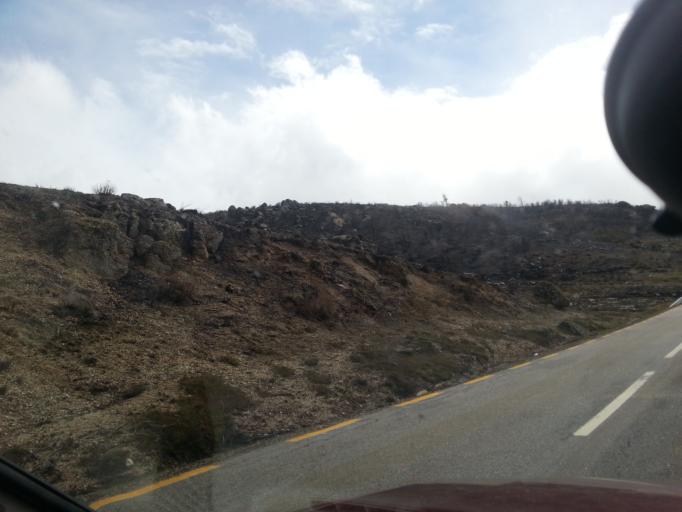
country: PT
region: Guarda
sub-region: Manteigas
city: Manteigas
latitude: 40.4194
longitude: -7.6011
